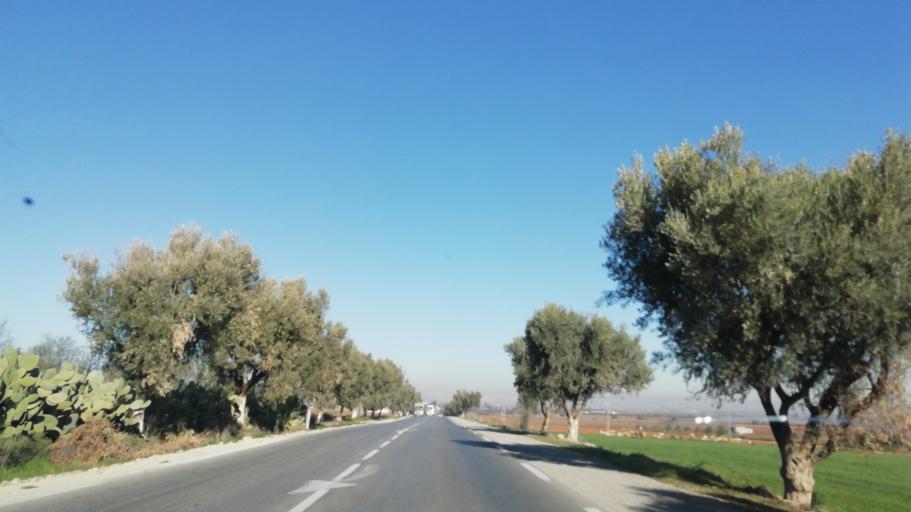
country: DZ
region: Mascara
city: Mascara
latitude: 35.2645
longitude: 0.1290
